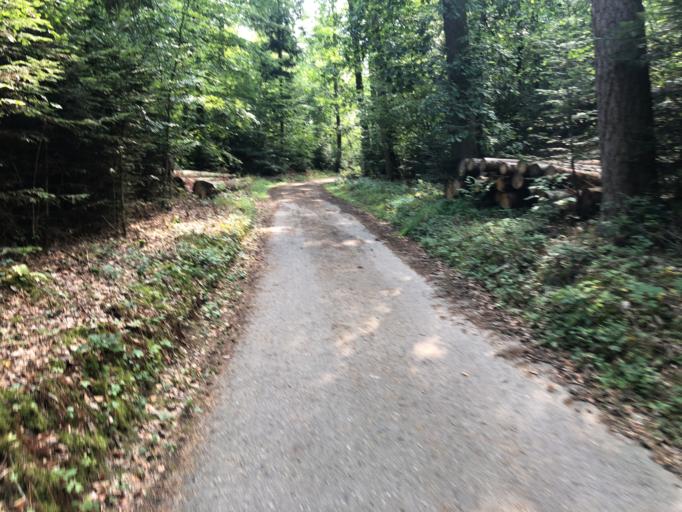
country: DE
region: Baden-Wuerttemberg
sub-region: Tuebingen Region
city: Rottenburg
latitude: 48.5144
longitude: 8.9411
